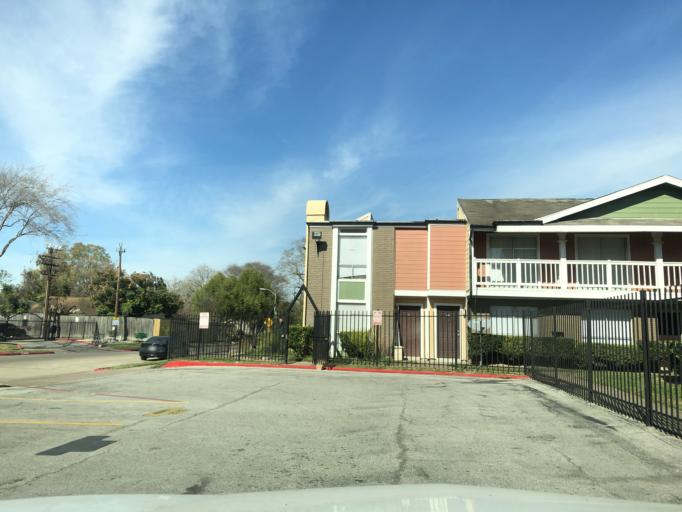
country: US
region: Texas
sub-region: Harris County
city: Bellaire
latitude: 29.6793
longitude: -95.5056
